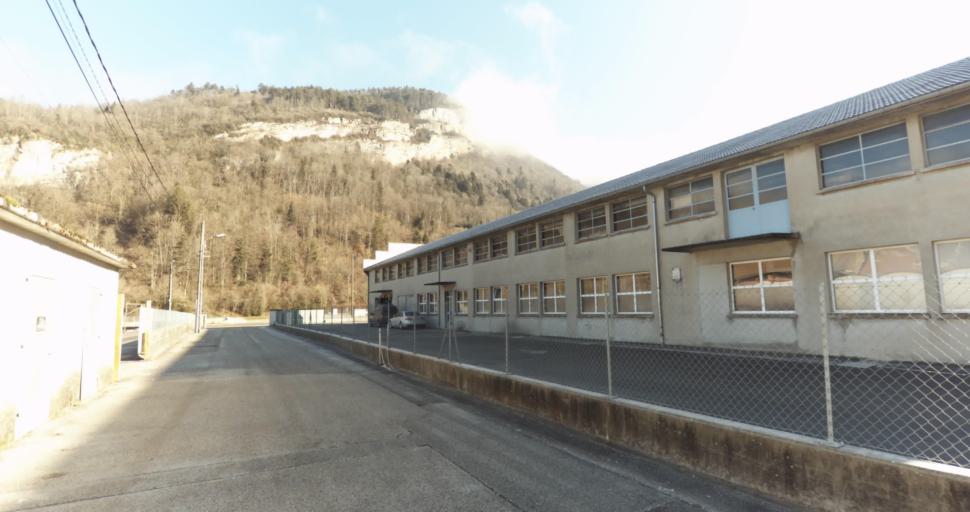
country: FR
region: Rhone-Alpes
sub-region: Departement de l'Ain
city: Nantua
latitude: 46.1447
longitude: 5.6132
